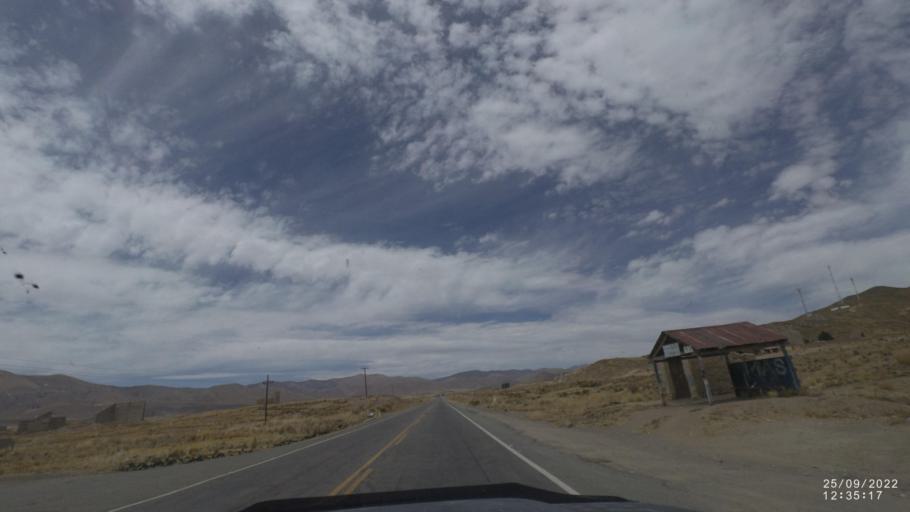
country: BO
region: Oruro
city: Machacamarca
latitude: -18.1634
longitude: -67.0071
